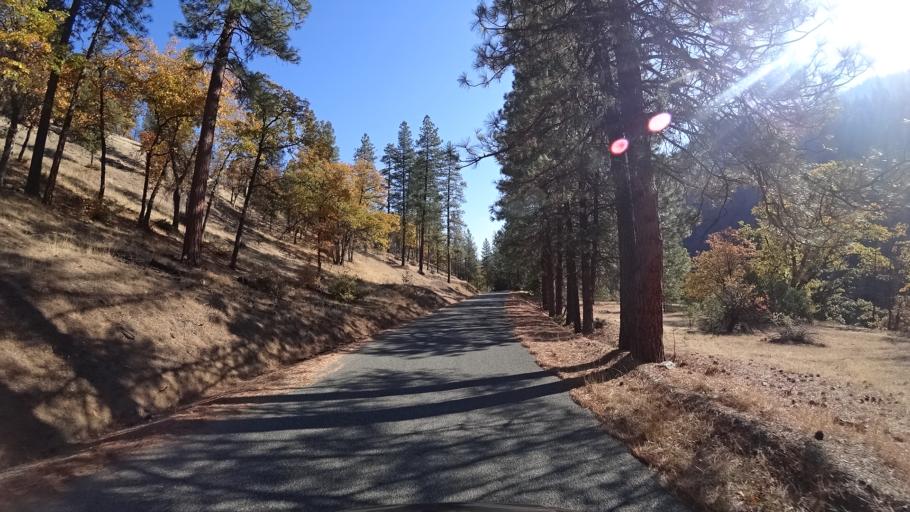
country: US
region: California
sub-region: Siskiyou County
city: Happy Camp
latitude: 41.6886
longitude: -123.0827
